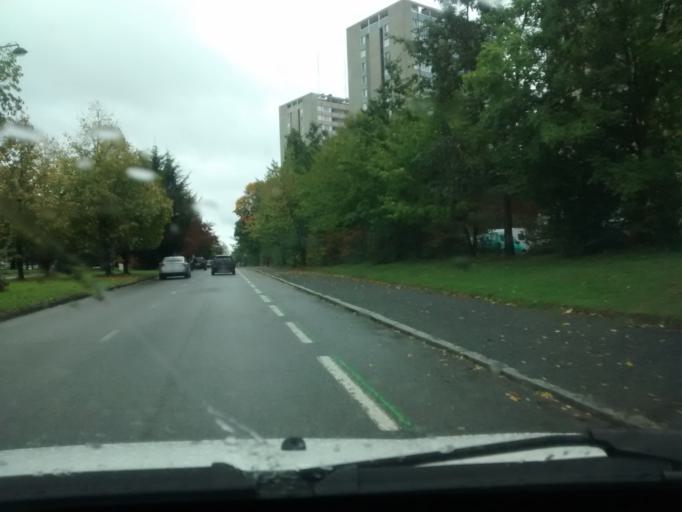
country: FR
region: Brittany
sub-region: Departement d'Ille-et-Vilaine
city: Rennes
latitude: 48.1282
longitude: -1.6623
